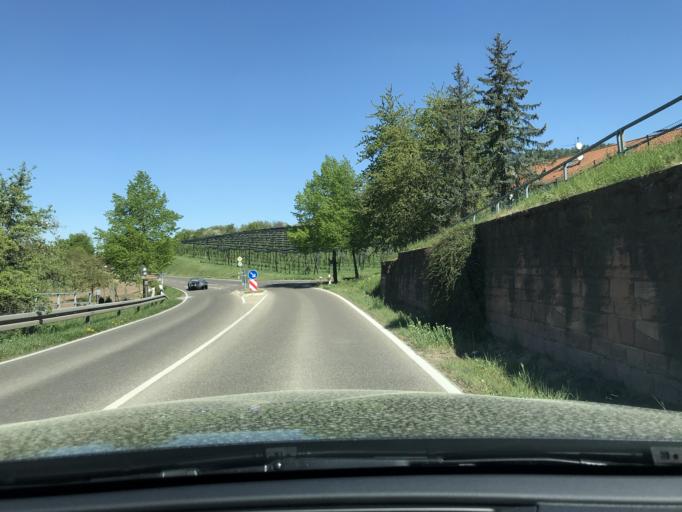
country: DE
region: Baden-Wuerttemberg
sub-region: Regierungsbezirk Stuttgart
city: Weinstadt-Endersbach
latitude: 48.8232
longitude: 9.3779
